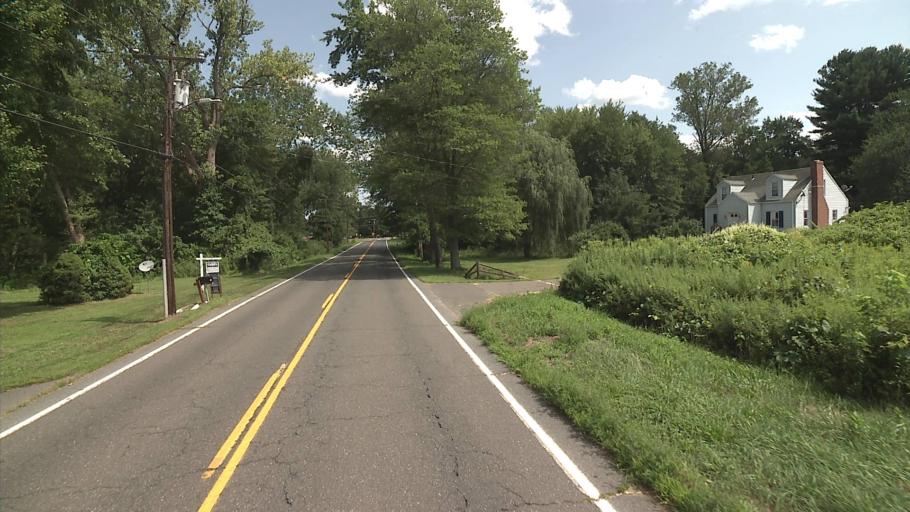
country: US
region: Connecticut
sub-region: Hartford County
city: Broad Brook
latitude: 41.8990
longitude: -72.5833
